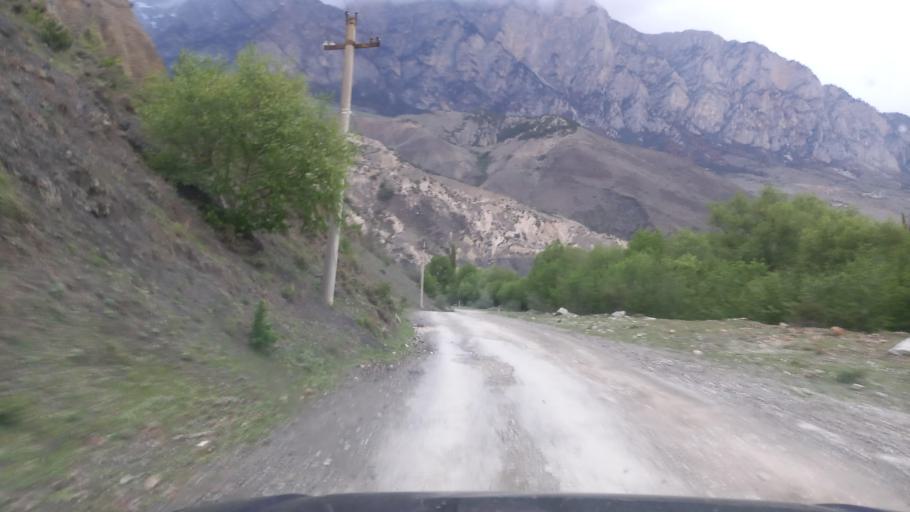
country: RU
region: North Ossetia
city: Mizur
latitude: 42.8568
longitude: 44.1493
